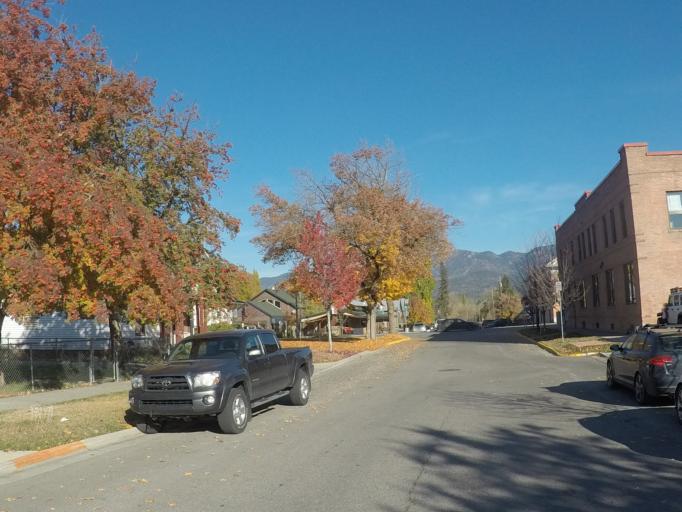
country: US
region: Montana
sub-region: Flathead County
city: Whitefish
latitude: 48.4100
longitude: -114.3396
